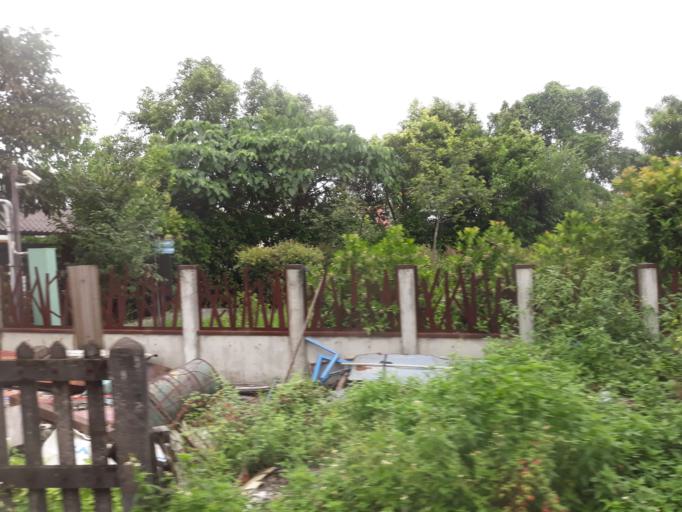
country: TW
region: Taiwan
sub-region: Yilan
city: Yilan
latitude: 24.6807
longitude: 121.7746
